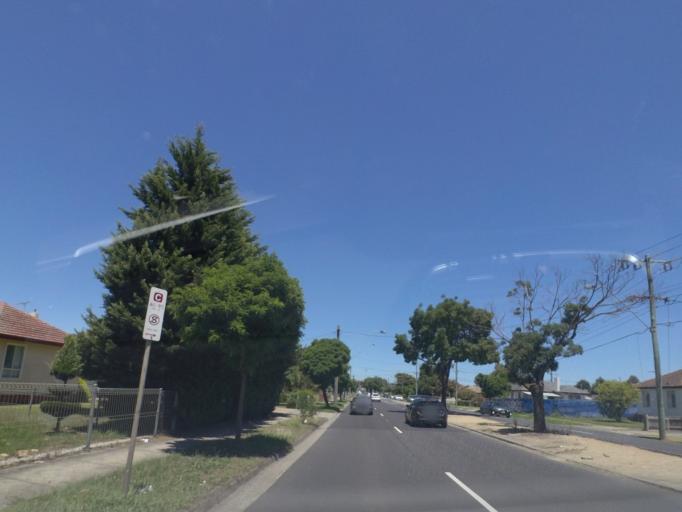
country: AU
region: Victoria
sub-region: Darebin
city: Kingsbury
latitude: -37.7281
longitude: 145.0260
